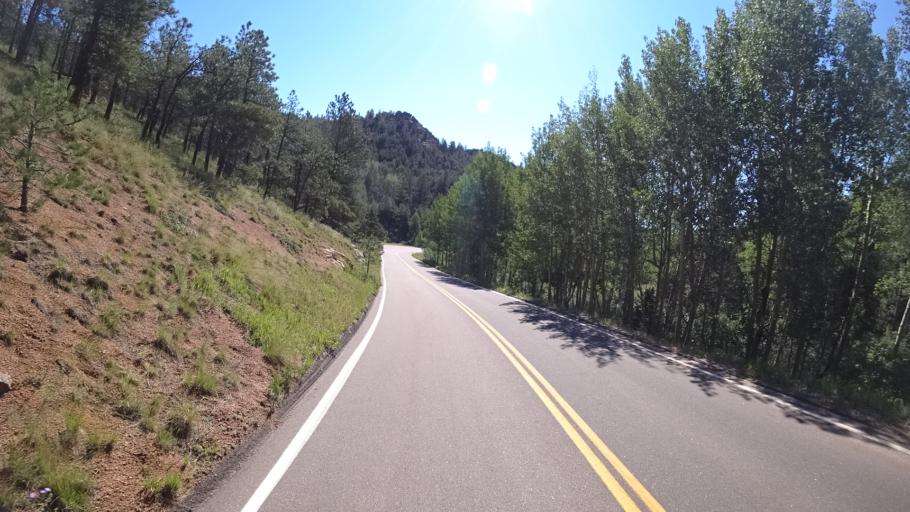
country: US
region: Colorado
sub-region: El Paso County
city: Cascade-Chipita Park
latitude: 38.9086
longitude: -105.0149
